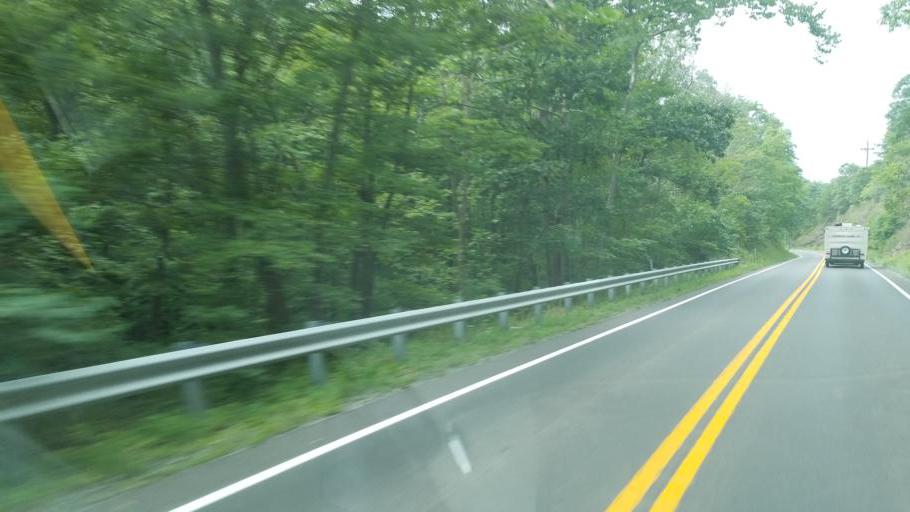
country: US
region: West Virginia
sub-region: Mineral County
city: Fort Ashby
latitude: 39.5426
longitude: -78.5061
